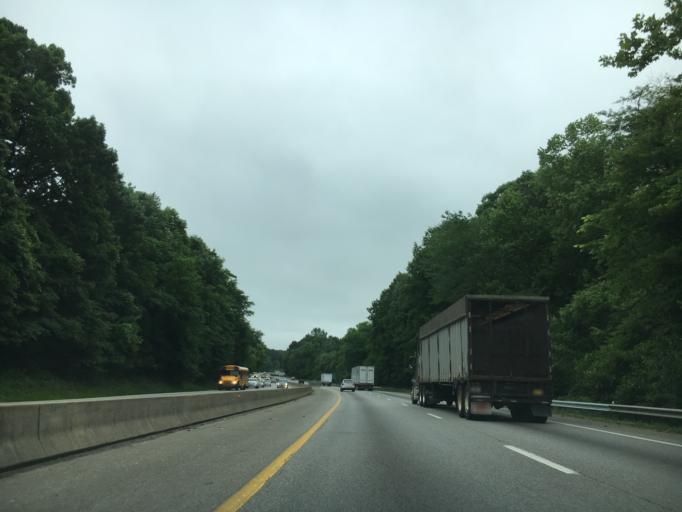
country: US
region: Virginia
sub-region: City of Petersburg
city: Petersburg
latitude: 37.2054
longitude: -77.4122
